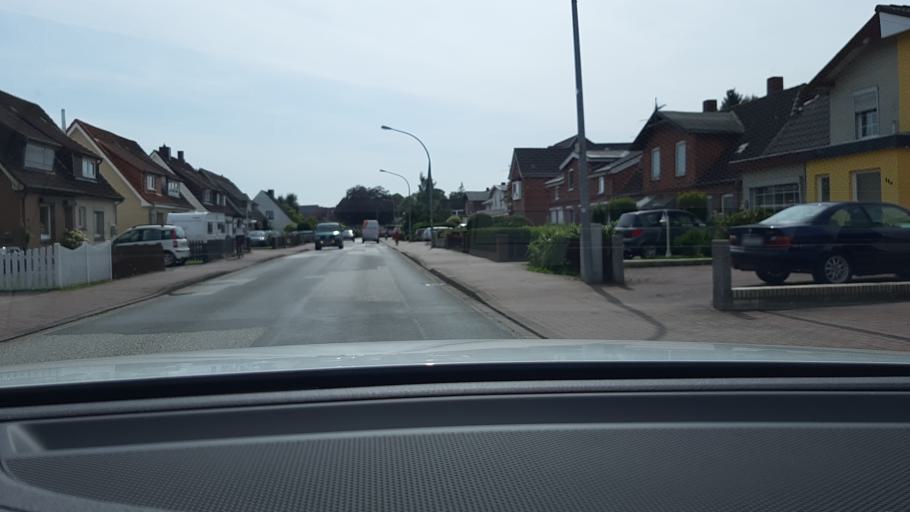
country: DE
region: Schleswig-Holstein
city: Stockelsdorf
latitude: 53.8918
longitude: 10.6509
